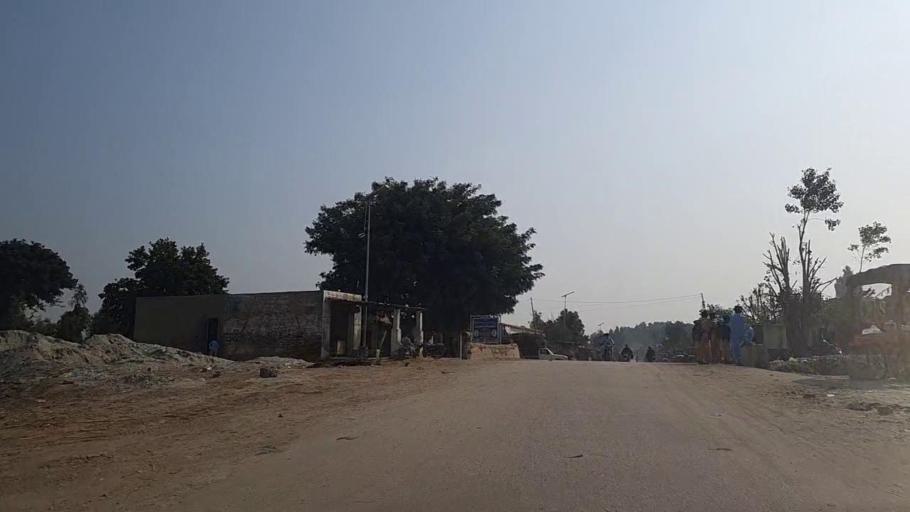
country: PK
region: Sindh
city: Jam Sahib
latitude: 26.3329
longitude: 68.5370
